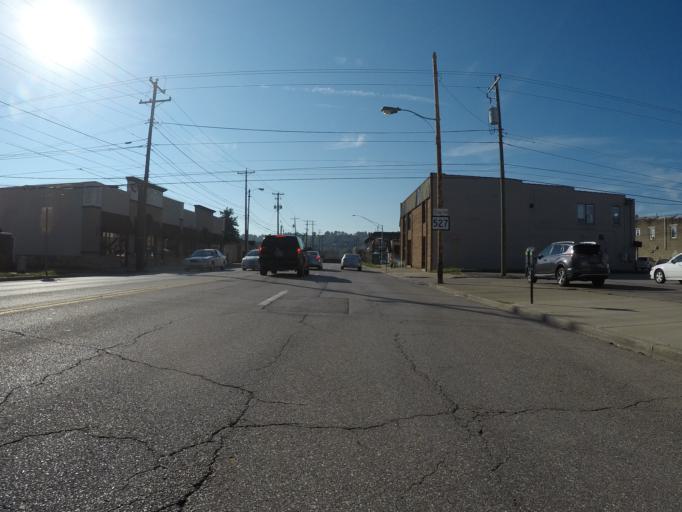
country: US
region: West Virginia
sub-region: Cabell County
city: Huntington
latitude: 38.4173
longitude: -82.4447
